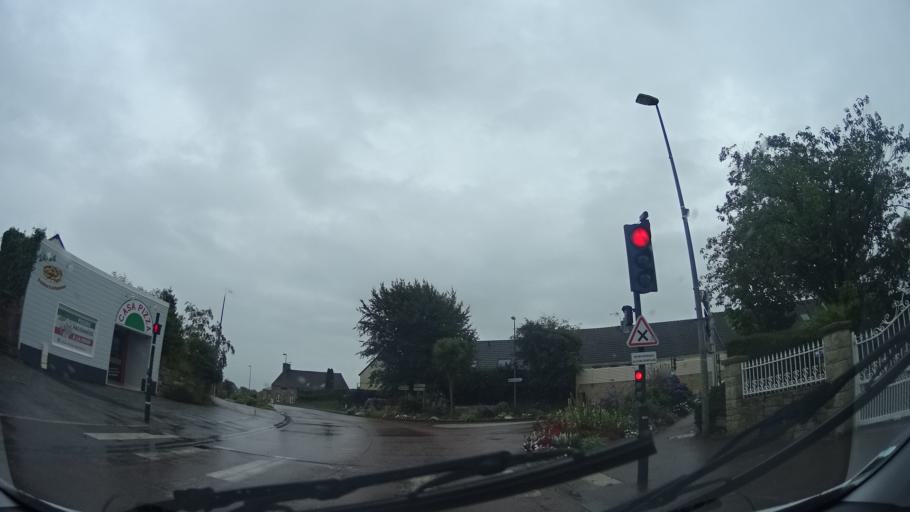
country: FR
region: Lower Normandy
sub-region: Departement de la Manche
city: Urville-Nacqueville
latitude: 49.5947
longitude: -1.7736
